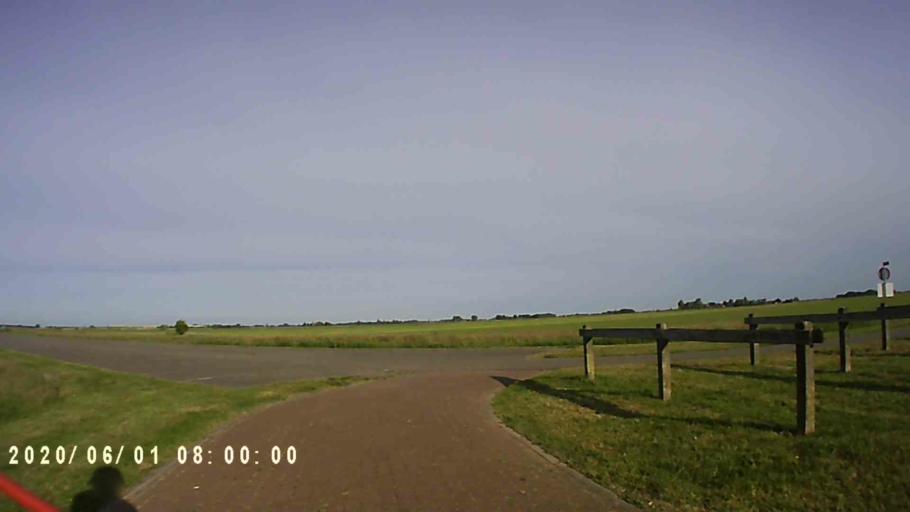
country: NL
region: Friesland
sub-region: Gemeente Dantumadiel
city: Rinsumageast
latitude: 53.2830
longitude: 5.9365
